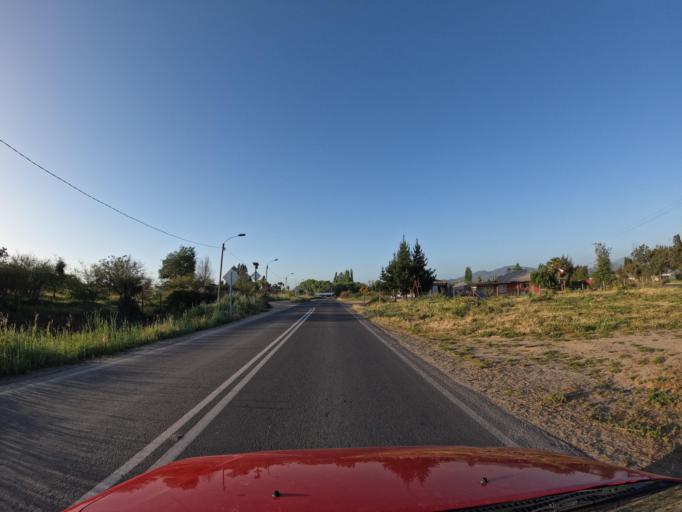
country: CL
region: O'Higgins
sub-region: Provincia de Cachapoal
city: San Vicente
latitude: -34.3150
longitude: -71.3853
